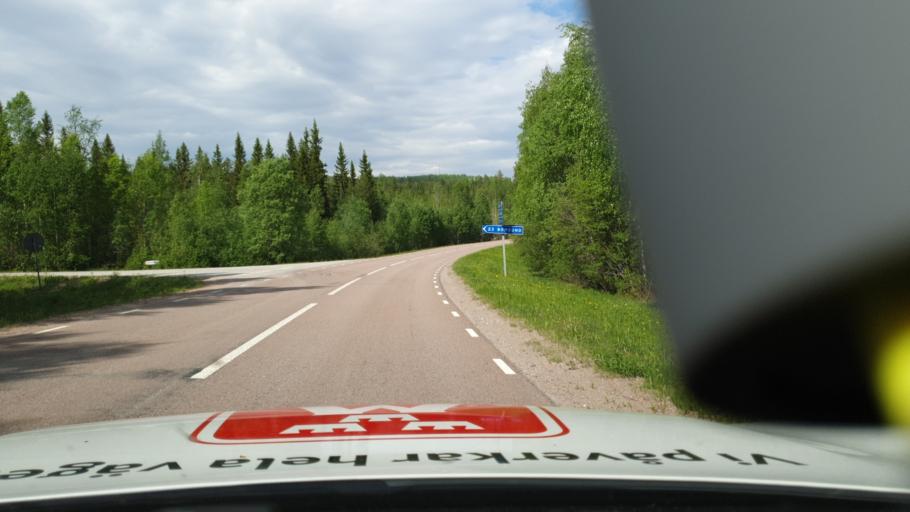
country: SE
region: Jaemtland
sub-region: Braecke Kommun
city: Braecke
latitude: 62.9598
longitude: 15.7477
